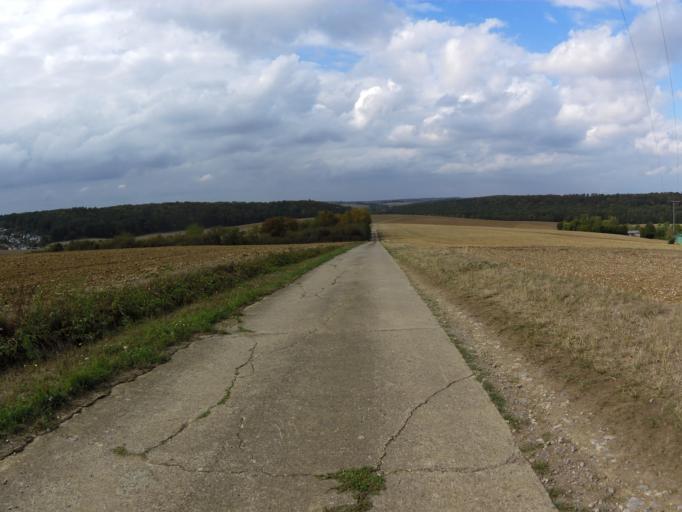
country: DE
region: Bavaria
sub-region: Regierungsbezirk Unterfranken
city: Eisingen
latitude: 49.7627
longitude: 9.8173
